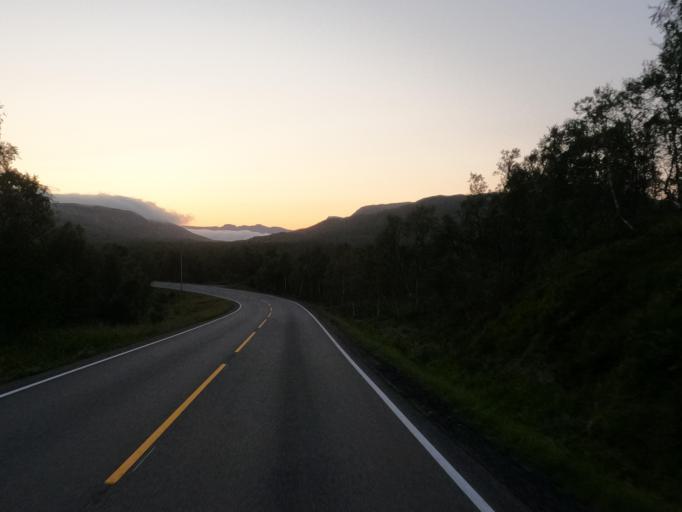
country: NO
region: Nordland
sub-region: Lodingen
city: Lodingen
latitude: 68.5145
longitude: 15.8768
